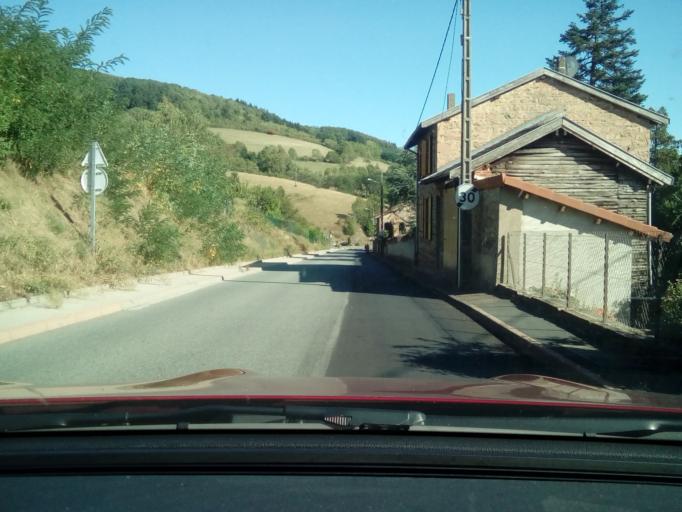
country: FR
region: Rhone-Alpes
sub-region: Departement du Rhone
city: Tarare
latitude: 45.9449
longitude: 4.4318
